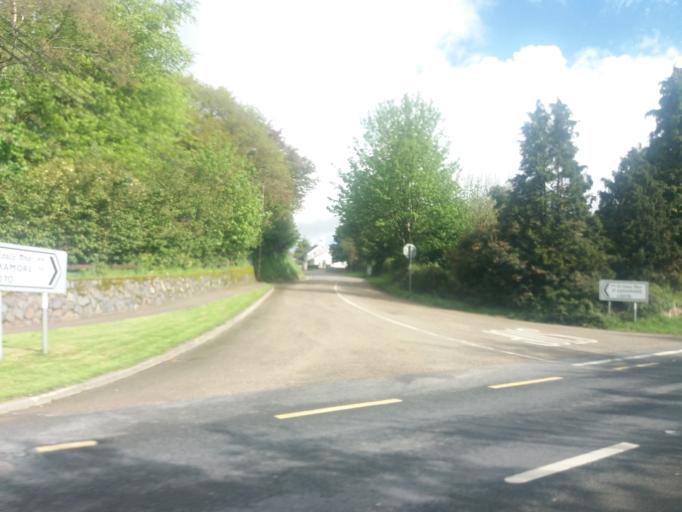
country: IE
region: Leinster
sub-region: Loch Garman
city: Ferns
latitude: 52.5922
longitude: -6.4896
